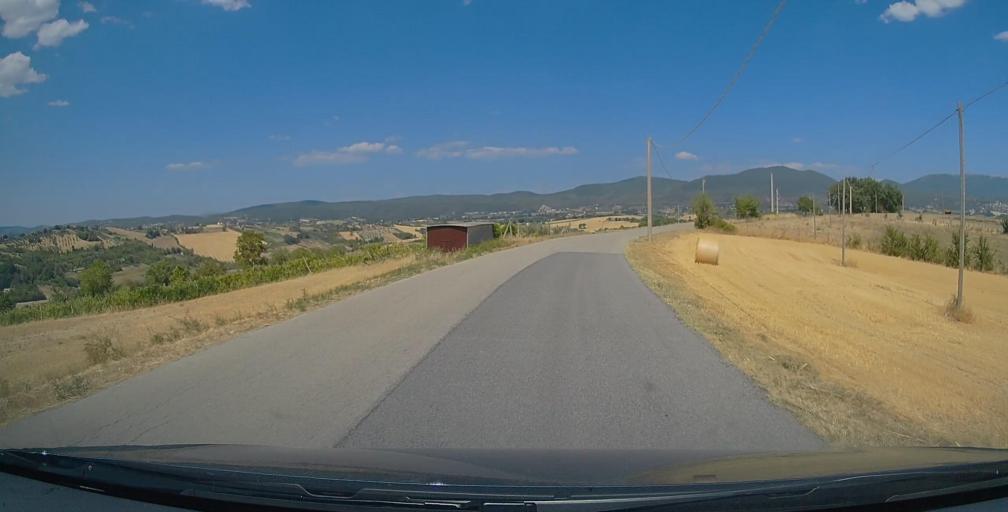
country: IT
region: Umbria
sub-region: Provincia di Terni
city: Otricoli
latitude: 42.4062
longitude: 12.4984
